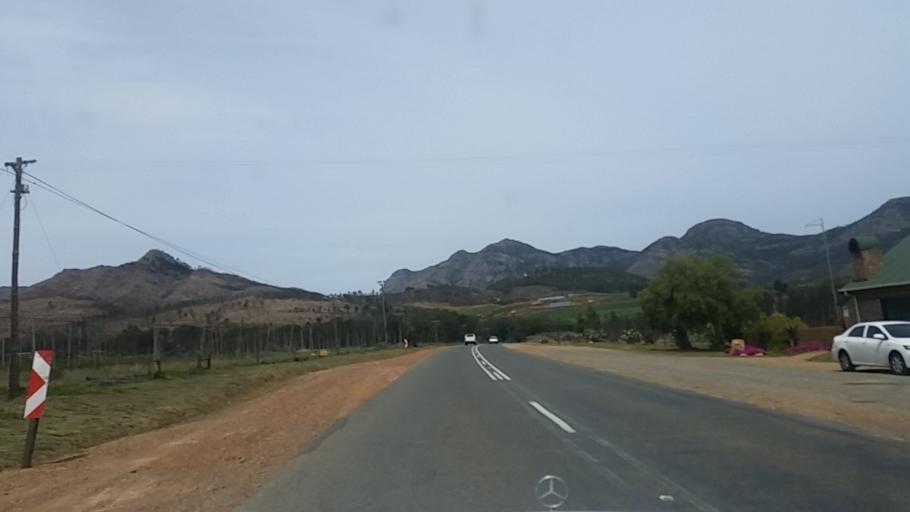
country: ZA
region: Western Cape
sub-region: Eden District Municipality
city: George
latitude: -33.8516
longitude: 22.3576
